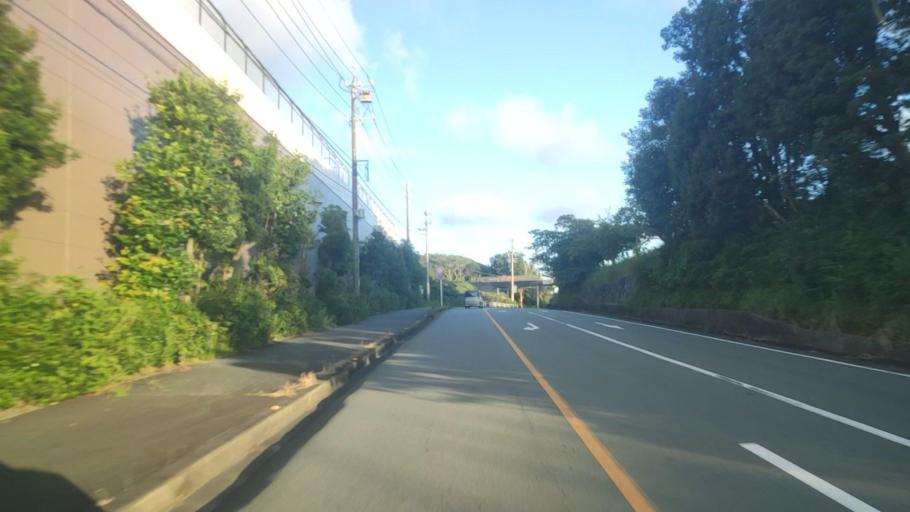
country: JP
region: Mie
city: Toba
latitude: 34.3230
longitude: 136.8281
